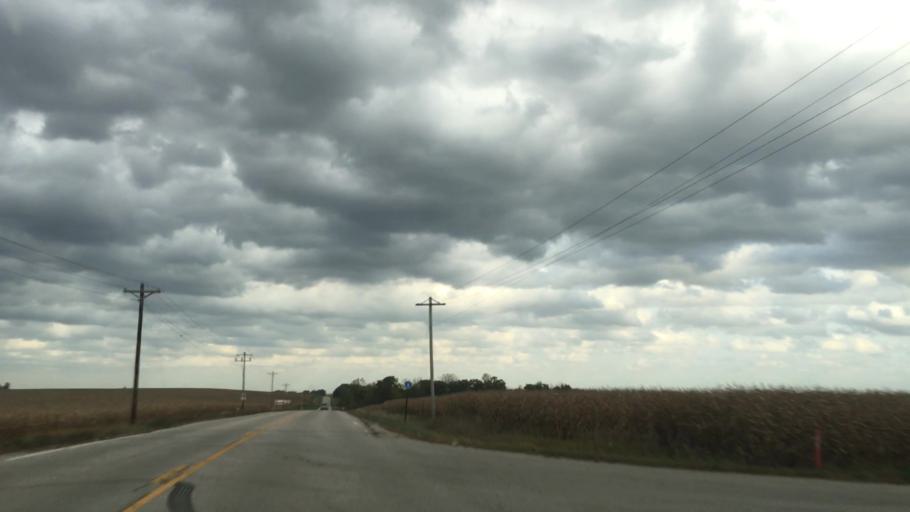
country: US
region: Minnesota
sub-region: Fillmore County
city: Preston
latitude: 43.7319
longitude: -92.0590
